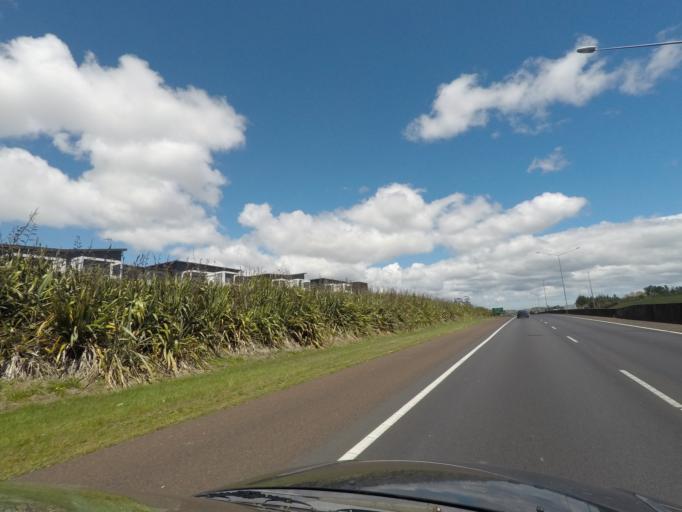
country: NZ
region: Auckland
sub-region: Auckland
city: Rosebank
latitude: -36.7955
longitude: 174.6470
